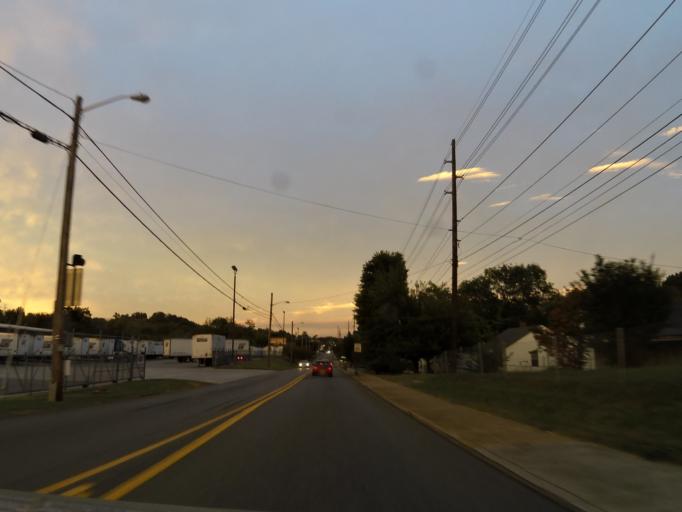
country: US
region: Tennessee
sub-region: Knox County
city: Knoxville
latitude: 35.9504
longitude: -83.9712
